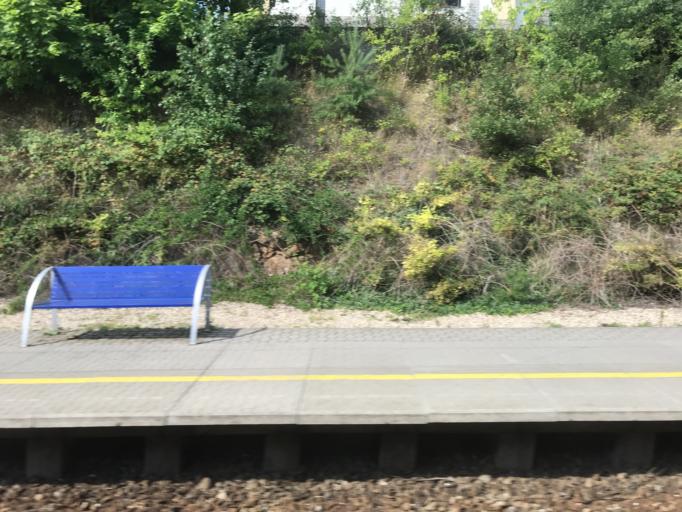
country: CZ
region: Central Bohemia
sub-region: Okres Praha-Vychod
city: Mnichovice
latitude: 49.9327
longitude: 14.7070
